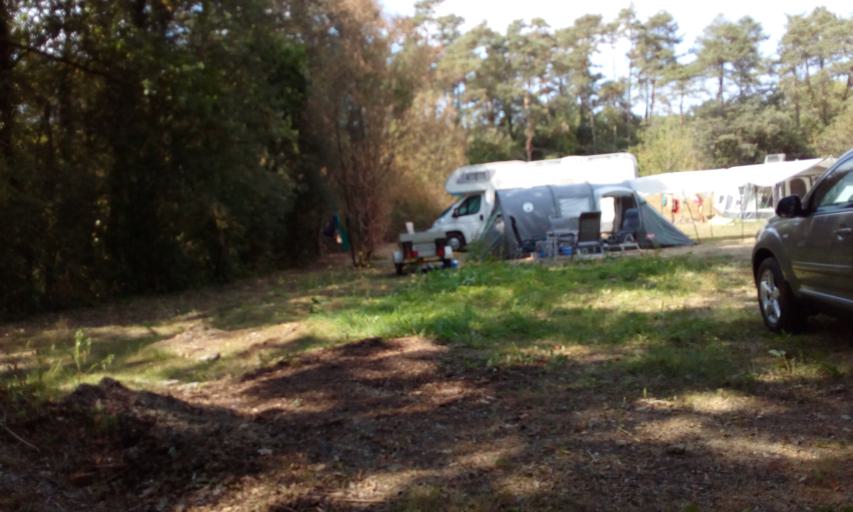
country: BE
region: Wallonia
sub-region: Province du Luxembourg
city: Wellin
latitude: 50.1105
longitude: 5.1339
